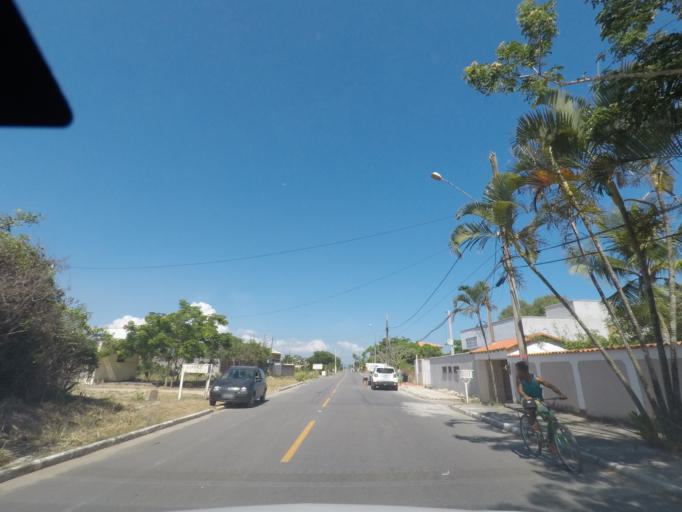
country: BR
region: Rio de Janeiro
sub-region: Marica
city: Marica
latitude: -22.9707
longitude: -42.9161
